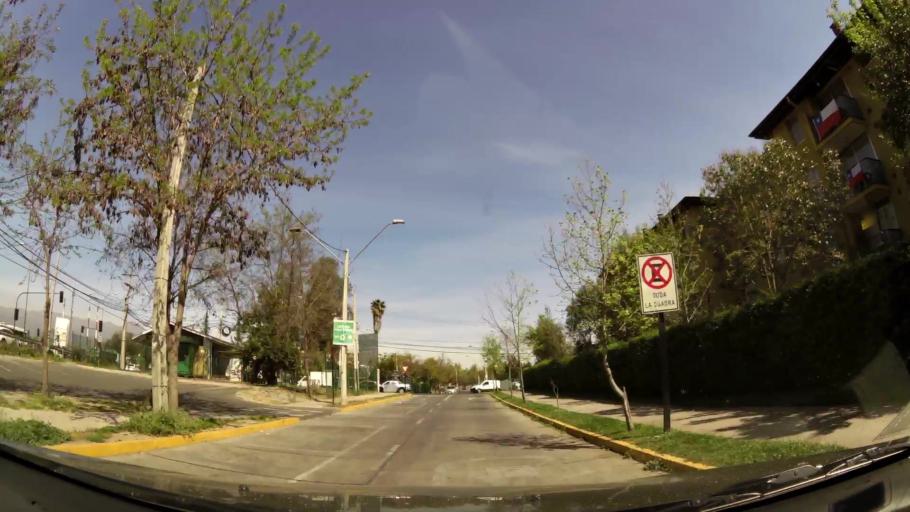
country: CL
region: Santiago Metropolitan
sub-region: Provincia de Cordillera
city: Puente Alto
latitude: -33.5659
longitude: -70.5555
